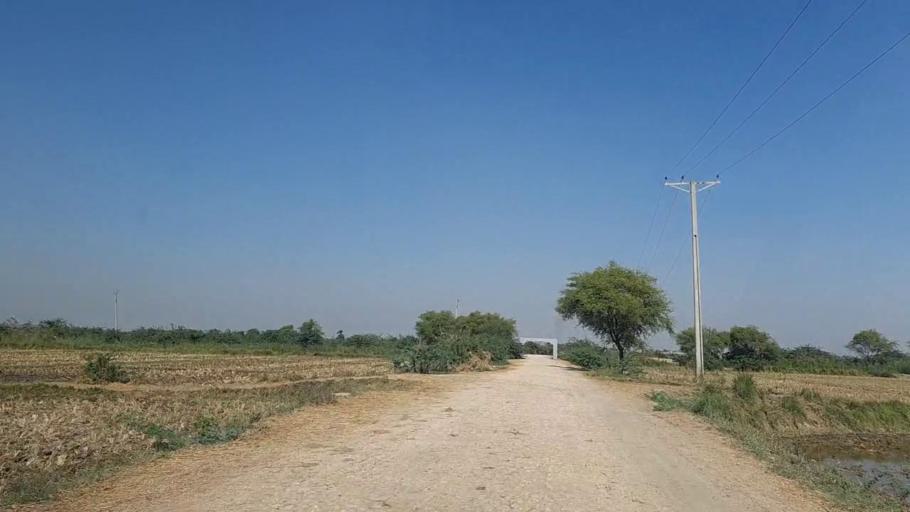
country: PK
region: Sindh
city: Daro Mehar
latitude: 24.7929
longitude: 68.1725
